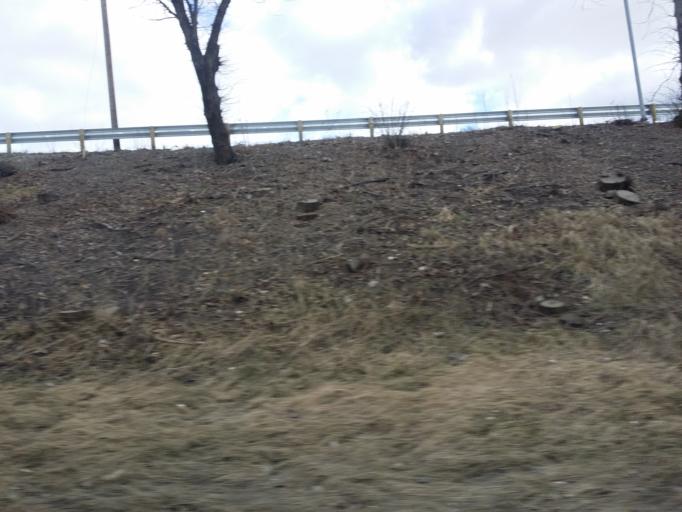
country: NO
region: Oslo
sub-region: Oslo
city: Oslo
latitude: 59.8970
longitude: 10.8117
